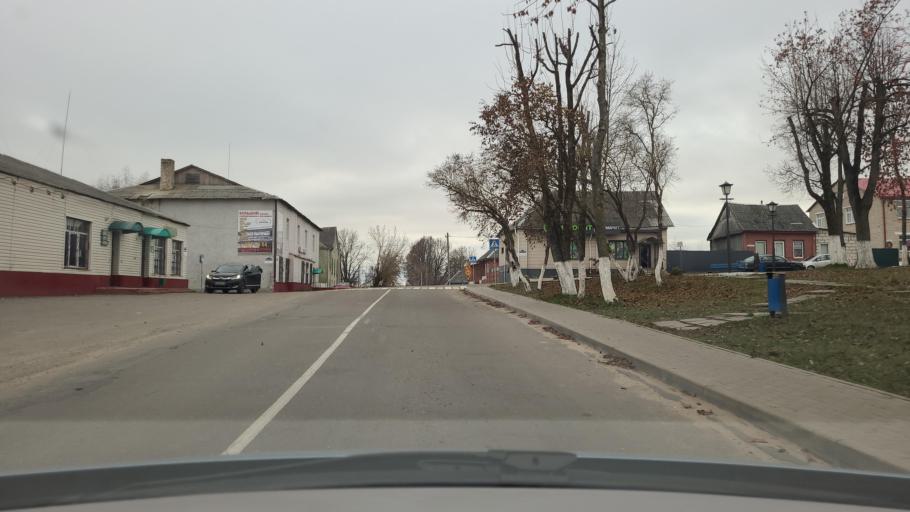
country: BY
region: Minsk
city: Khalopyenichy
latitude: 54.5178
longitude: 28.9610
